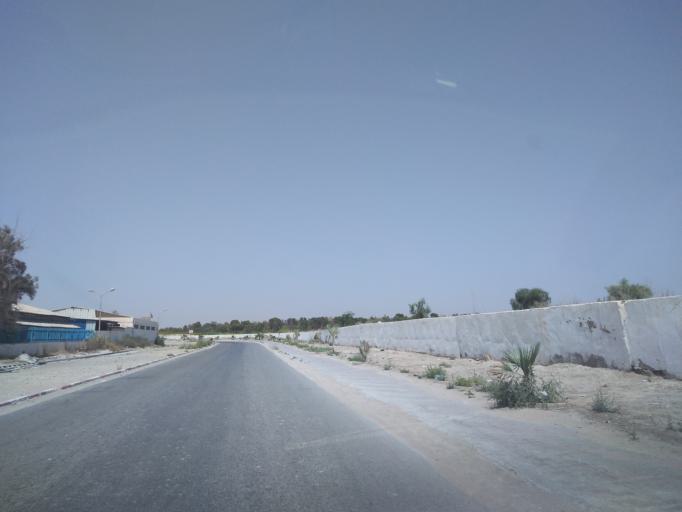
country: TN
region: Safaqis
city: Sfax
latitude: 34.7312
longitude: 10.7773
